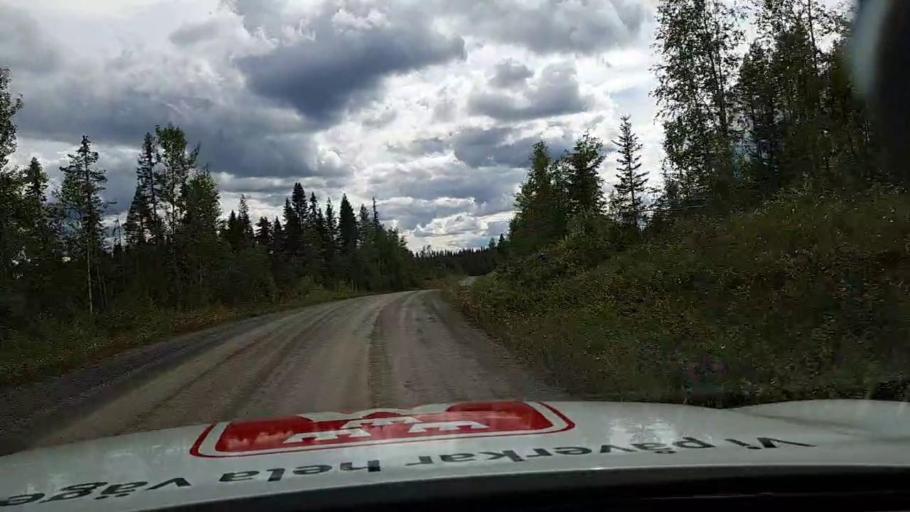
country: SE
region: Jaemtland
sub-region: Braecke Kommun
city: Braecke
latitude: 63.2675
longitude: 15.3786
